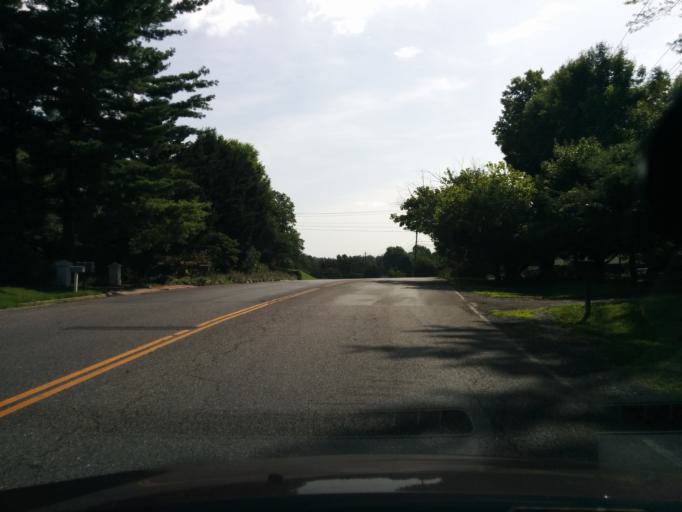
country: US
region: Virginia
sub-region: City of Lexington
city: Lexington
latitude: 37.7683
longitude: -79.4545
